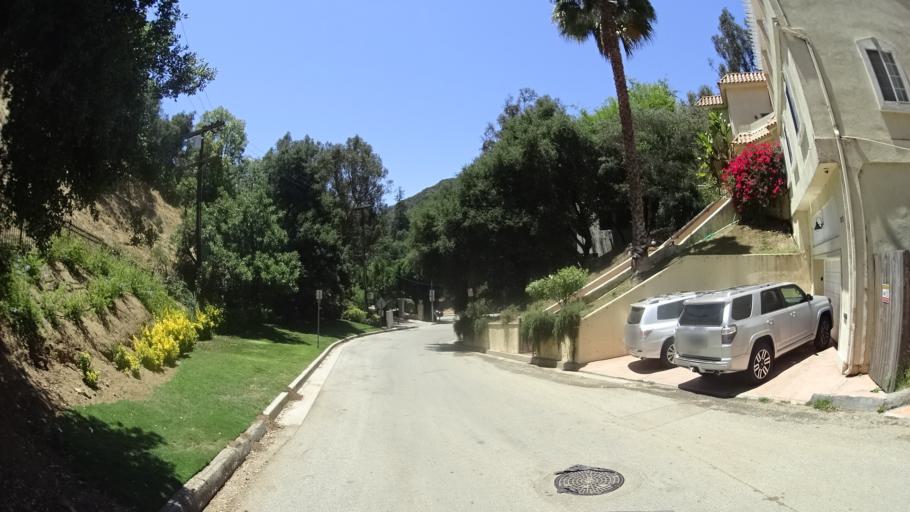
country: US
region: California
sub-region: Los Angeles County
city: West Hollywood
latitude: 34.1158
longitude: -118.3737
